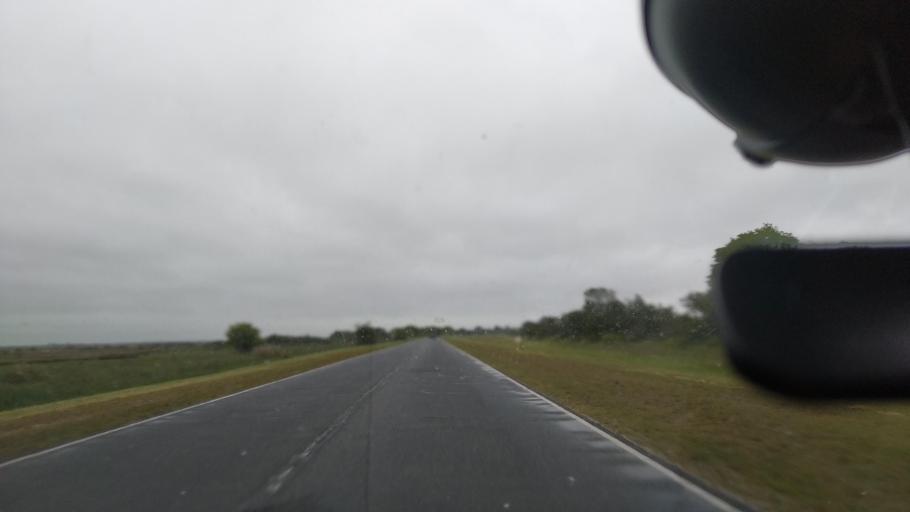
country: AR
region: Buenos Aires
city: Veronica
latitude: -35.7599
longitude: -57.3885
